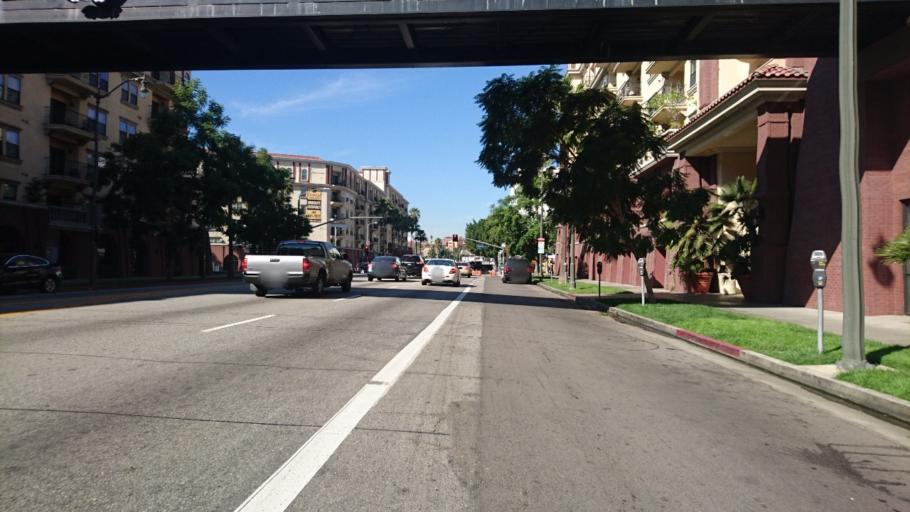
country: US
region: California
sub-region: Los Angeles County
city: Los Angeles
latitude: 34.0621
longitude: -118.2456
